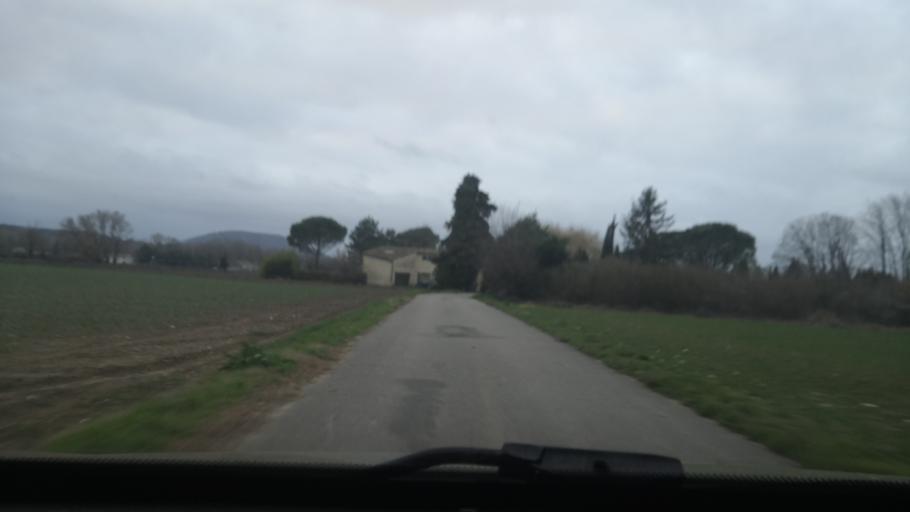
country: FR
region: Rhone-Alpes
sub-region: Departement de la Drome
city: Montboucher-sur-Jabron
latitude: 44.5525
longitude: 4.8416
